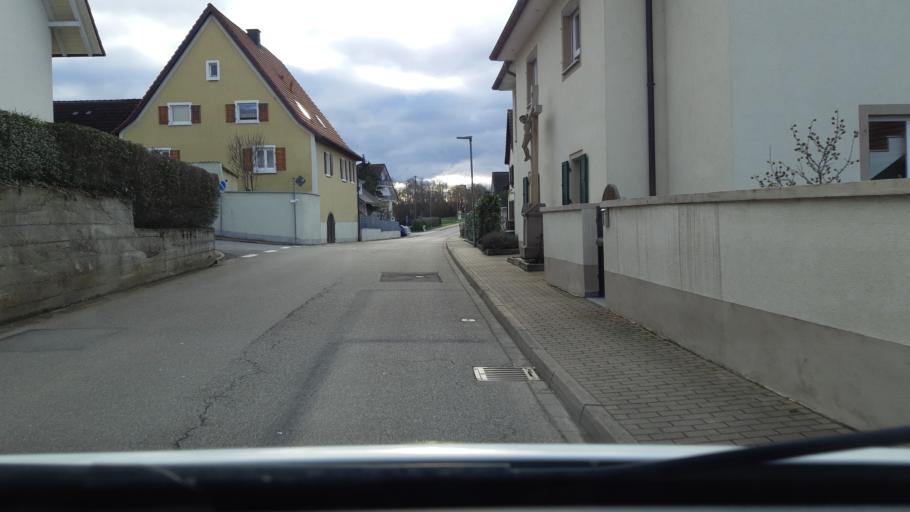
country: DE
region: Baden-Wuerttemberg
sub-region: Freiburg Region
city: Unterkrozingen
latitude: 47.9370
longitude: 7.6886
